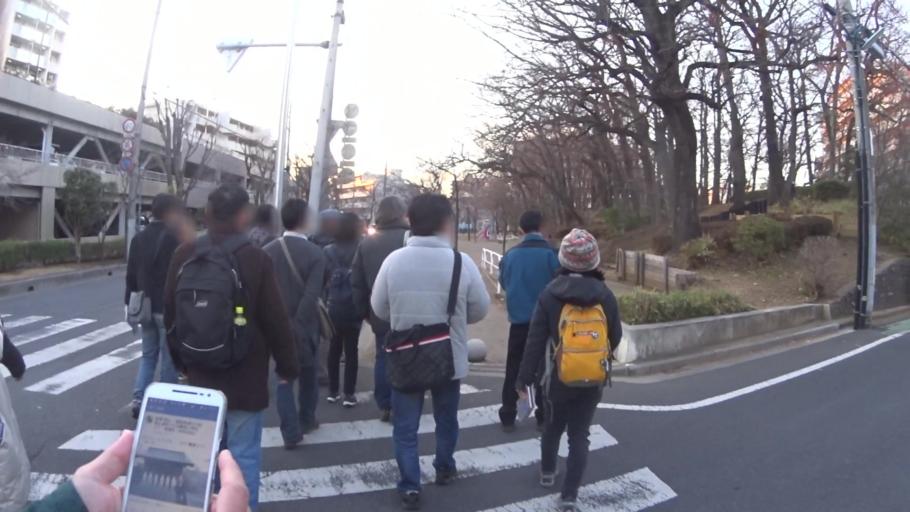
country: JP
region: Saitama
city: Shimotoda
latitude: 35.8469
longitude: 139.6762
